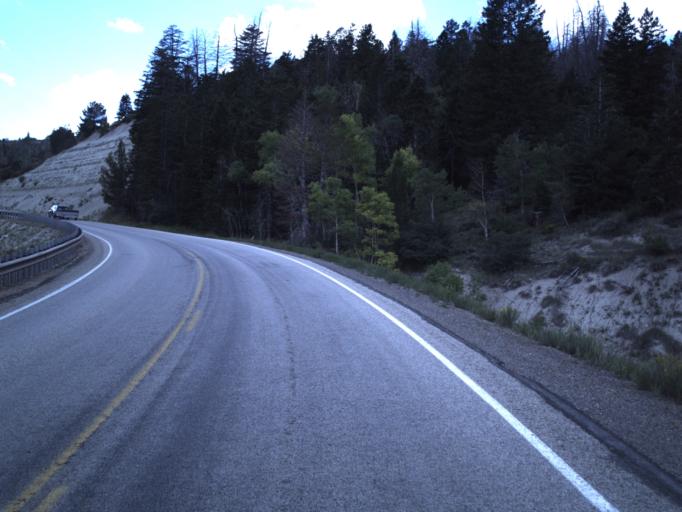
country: US
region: Utah
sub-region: Carbon County
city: Helper
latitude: 39.9015
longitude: -110.7420
